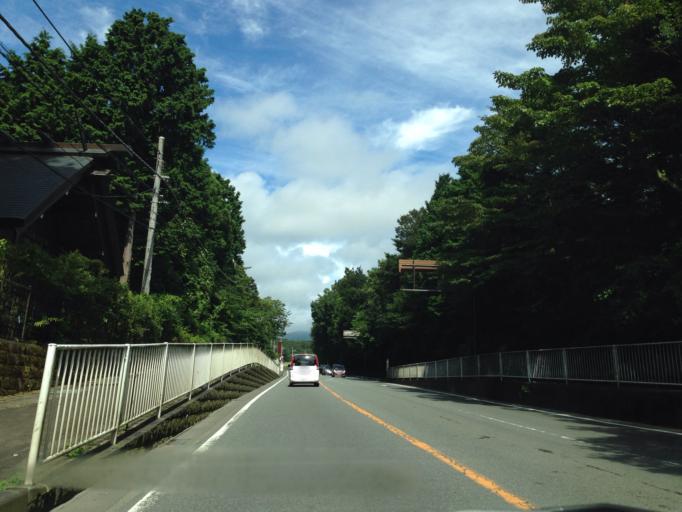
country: JP
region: Shizuoka
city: Gotemba
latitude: 35.3394
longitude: 138.8907
